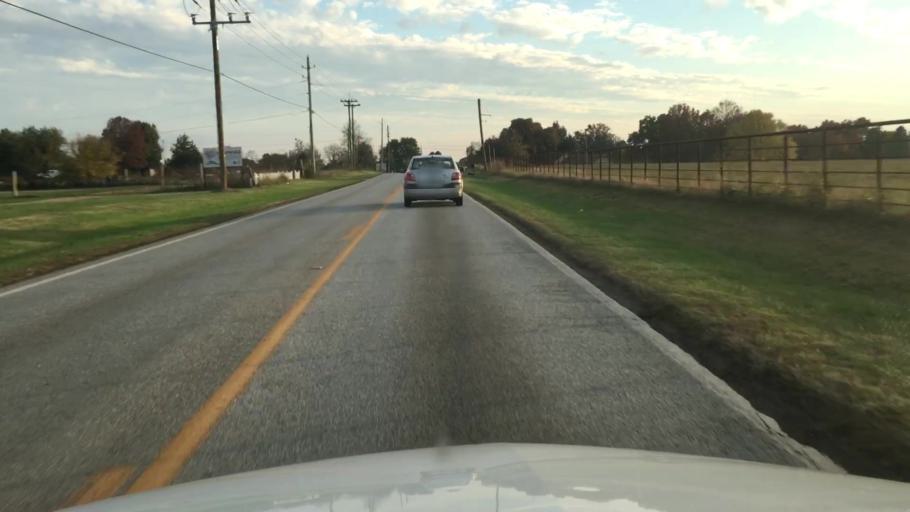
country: US
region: Arkansas
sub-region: Washington County
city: Elm Springs
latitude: 36.2217
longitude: -94.2304
